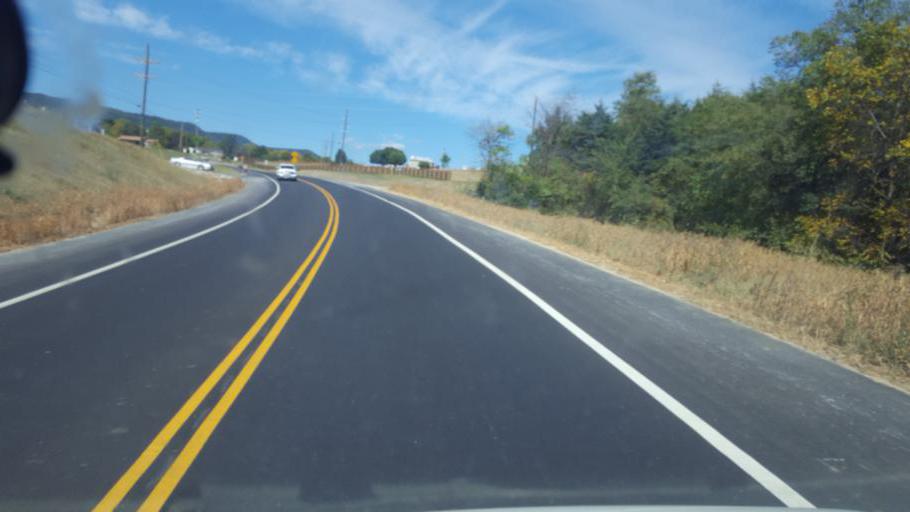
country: US
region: Virginia
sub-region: Page County
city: Shenandoah
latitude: 38.5549
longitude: -78.6061
